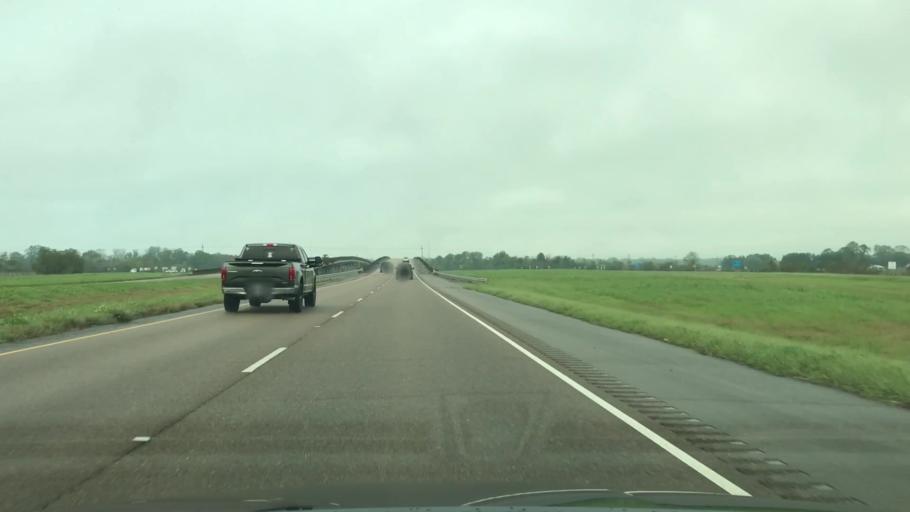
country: US
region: Louisiana
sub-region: Terrebonne Parish
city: Gray
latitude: 29.6832
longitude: -90.7459
